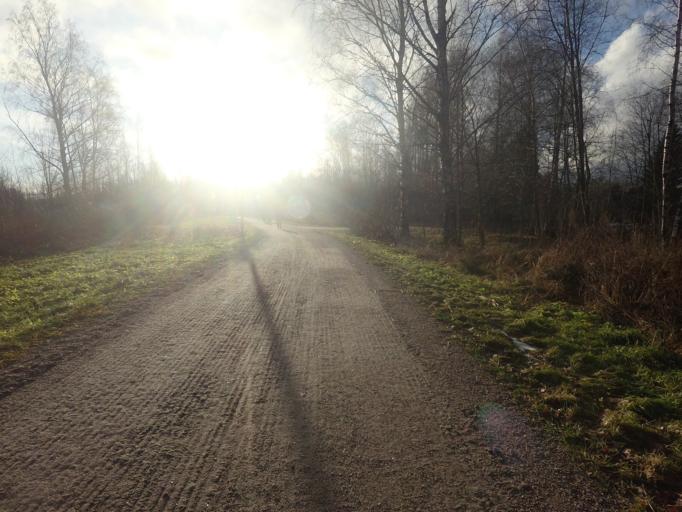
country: FI
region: Uusimaa
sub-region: Helsinki
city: Kilo
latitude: 60.2001
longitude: 24.7737
